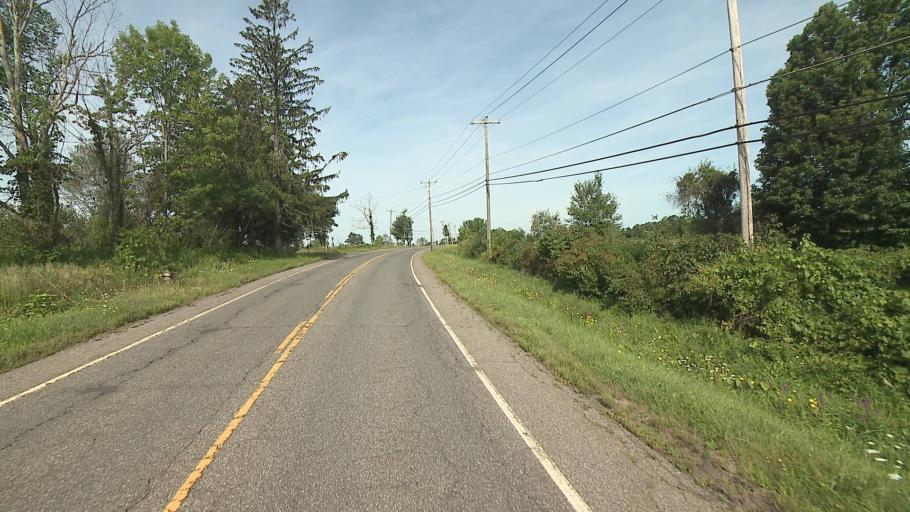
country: US
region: Connecticut
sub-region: Litchfield County
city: Thomaston
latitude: 41.7055
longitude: -73.1285
